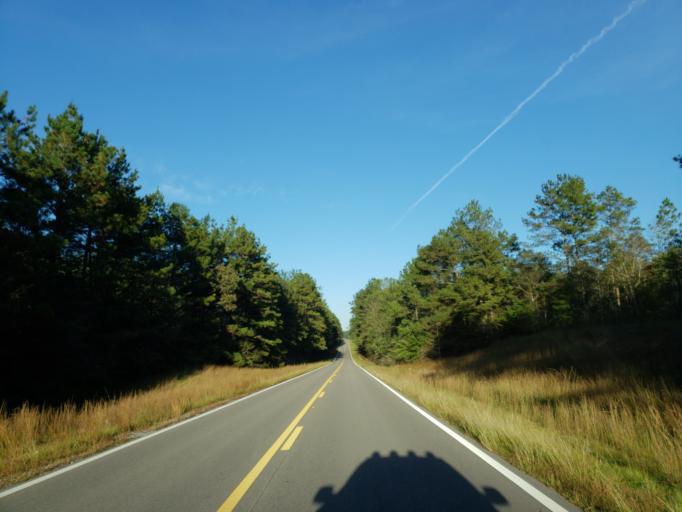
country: US
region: Mississippi
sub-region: Perry County
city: Richton
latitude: 31.3586
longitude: -88.7363
